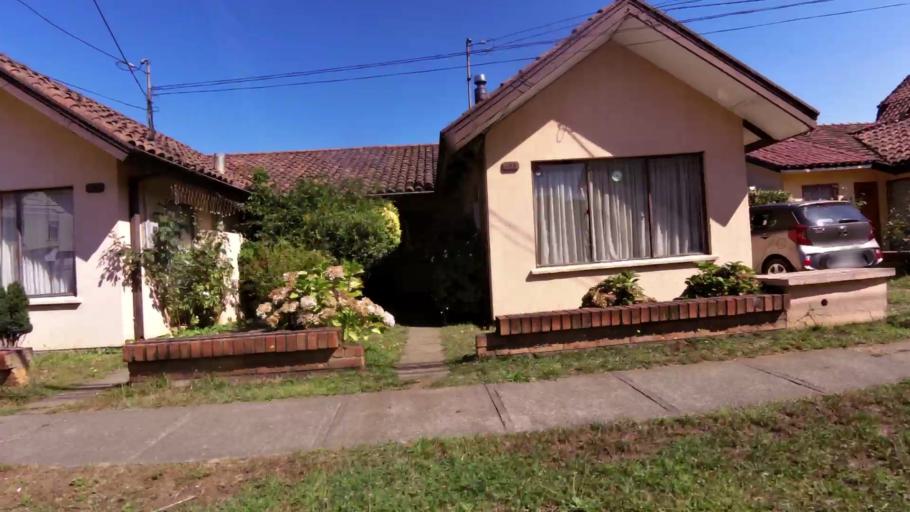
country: CL
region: Biobio
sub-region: Provincia de Concepcion
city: Concepcion
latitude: -36.7965
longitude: -73.0524
